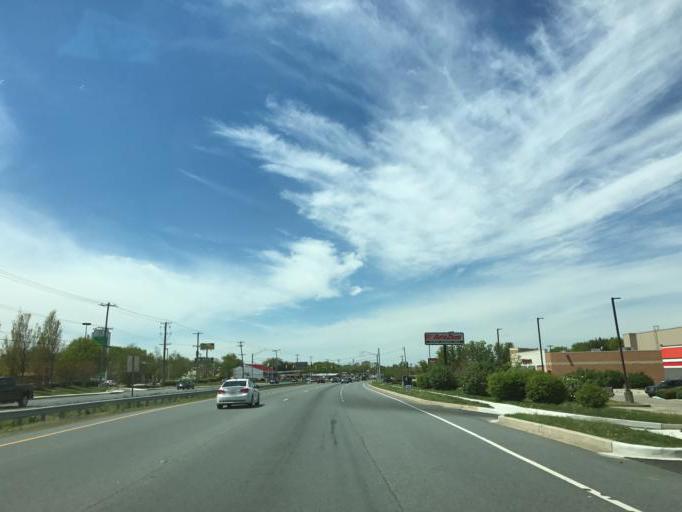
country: US
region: Maryland
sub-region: Cecil County
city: Elkton
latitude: 39.5982
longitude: -75.8175
